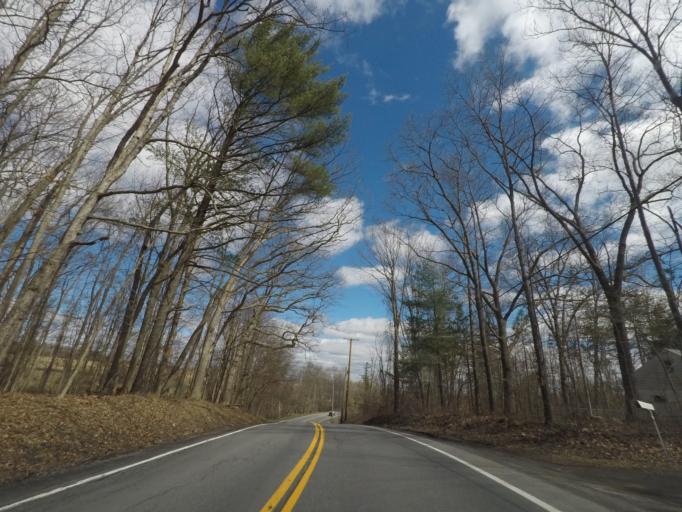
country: US
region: New York
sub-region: Albany County
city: Voorheesville
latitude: 42.5701
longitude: -73.9126
